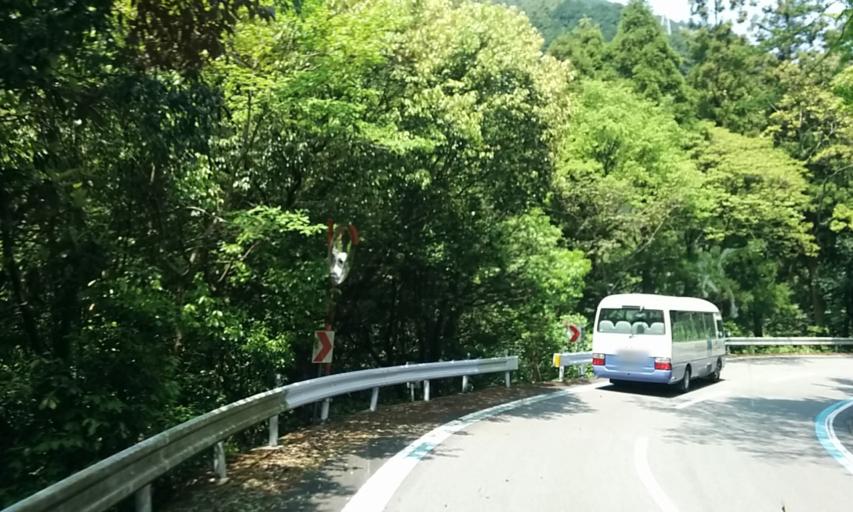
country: JP
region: Ehime
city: Niihama
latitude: 33.8982
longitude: 133.3082
